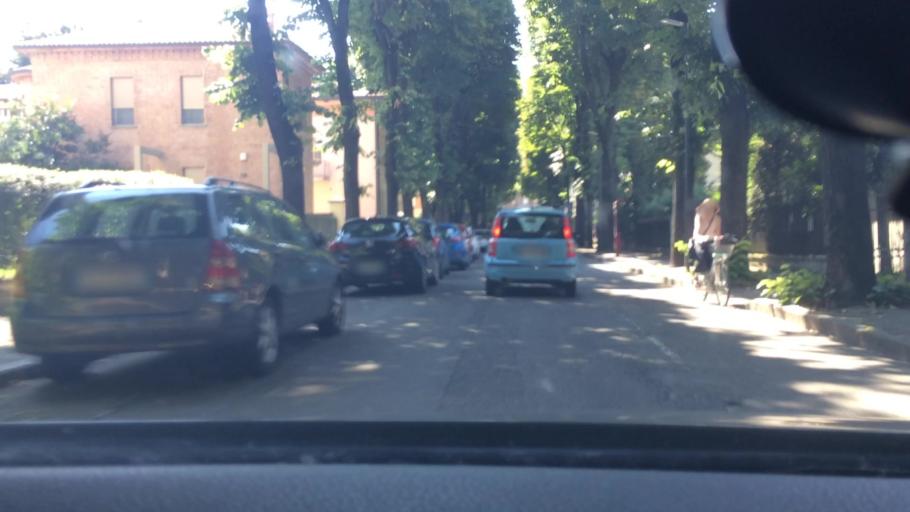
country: IT
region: Emilia-Romagna
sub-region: Provincia di Piacenza
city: Piacenza
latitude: 45.0463
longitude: 9.6818
